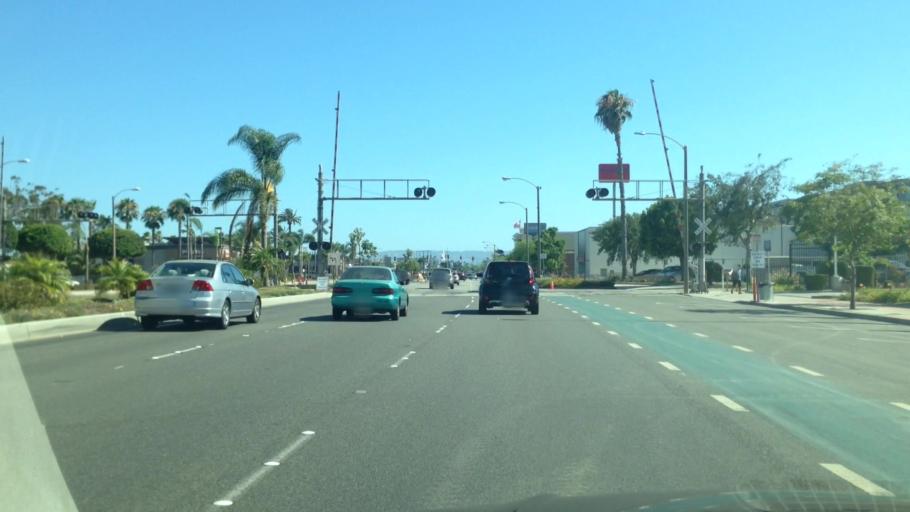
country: US
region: California
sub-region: Los Angeles County
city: Hawthorne
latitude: 33.9197
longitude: -118.3527
